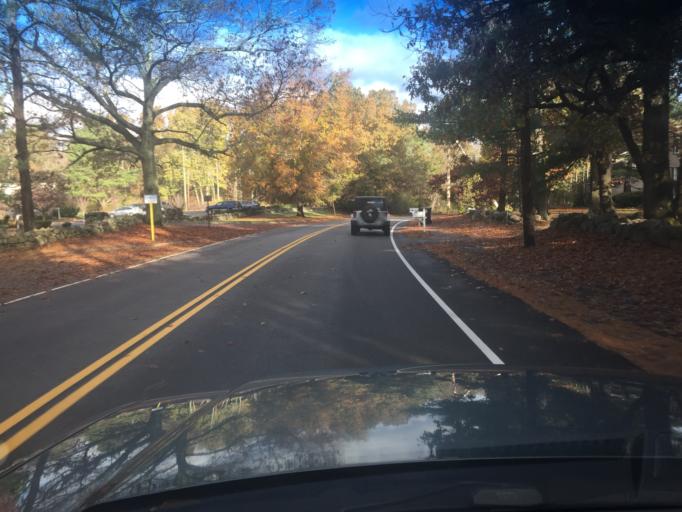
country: US
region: Massachusetts
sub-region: Norfolk County
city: Medfield
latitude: 42.1860
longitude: -71.3345
